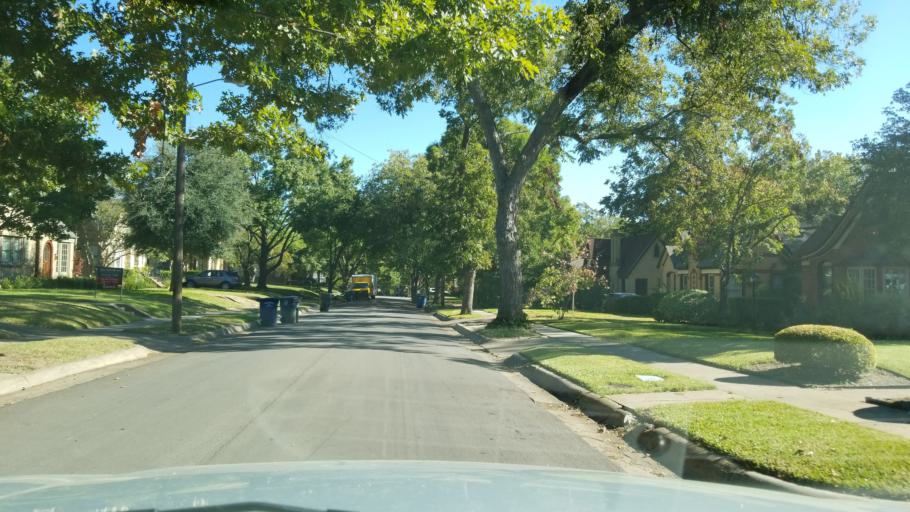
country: US
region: Texas
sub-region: Dallas County
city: Highland Park
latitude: 32.8035
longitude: -96.7447
